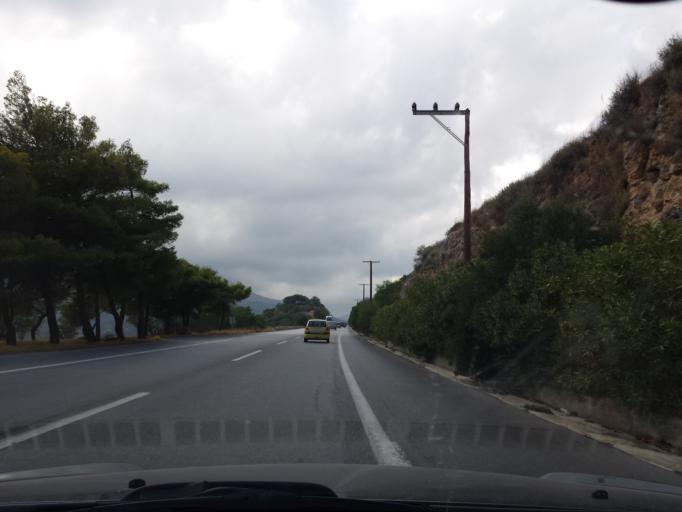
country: GR
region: Crete
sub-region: Nomos Lasithiou
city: Neapoli
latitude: 35.2497
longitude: 25.6331
